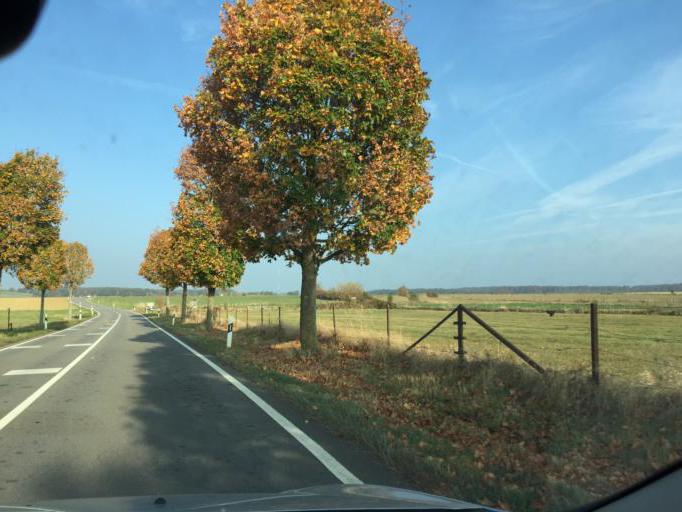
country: LU
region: Grevenmacher
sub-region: Canton de Remich
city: Dalheim
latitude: 49.5368
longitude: 6.2434
